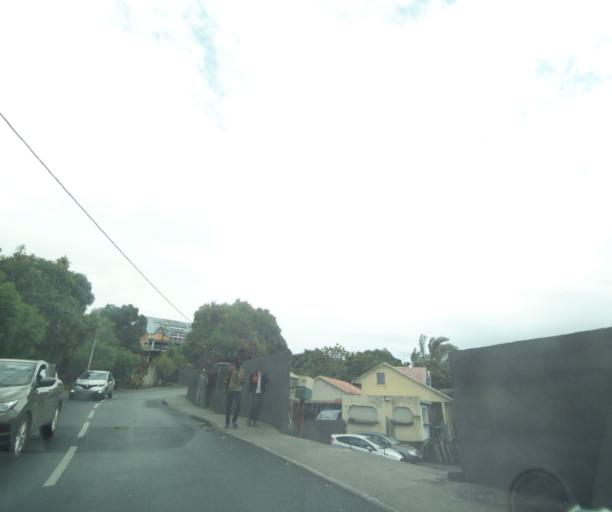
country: RE
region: Reunion
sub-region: Reunion
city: Saint-Paul
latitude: -21.0227
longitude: 55.2876
